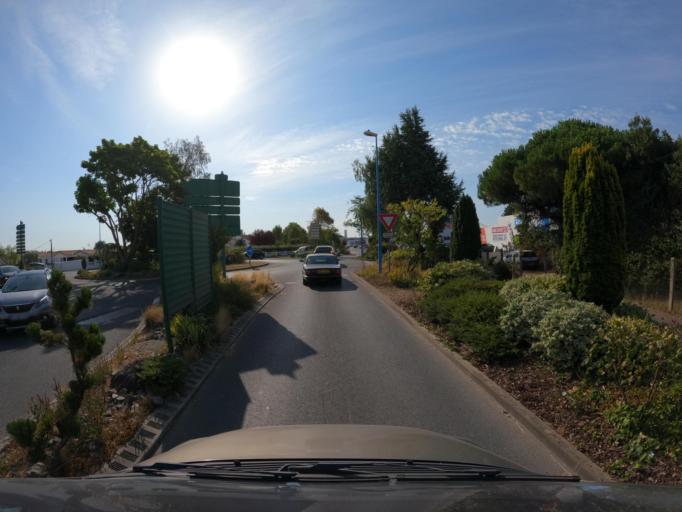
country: FR
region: Pays de la Loire
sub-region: Departement de la Vendee
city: Saint-Jean-de-Monts
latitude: 46.7967
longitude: -2.0701
